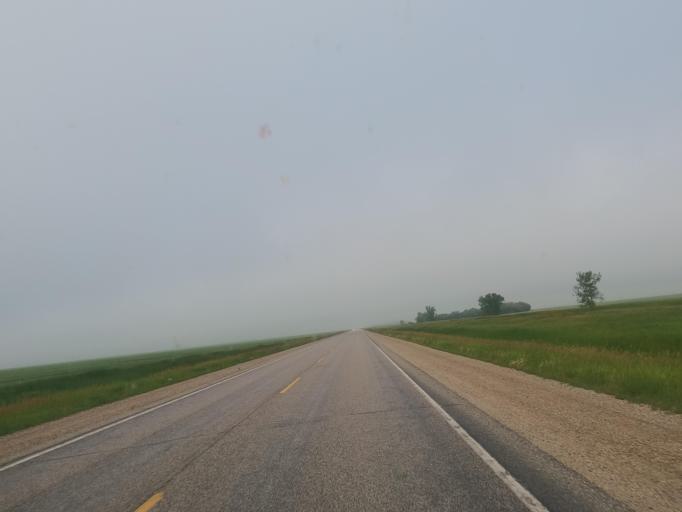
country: CA
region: Manitoba
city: Carman
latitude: 49.7271
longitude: -97.8699
